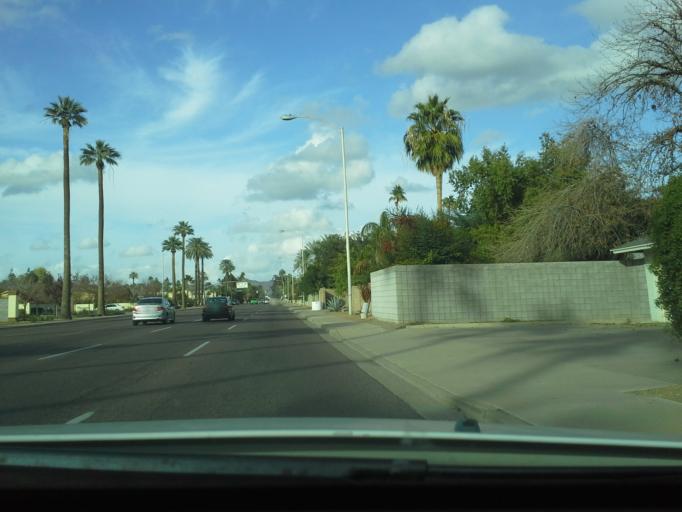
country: US
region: Arizona
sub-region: Maricopa County
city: Phoenix
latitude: 33.5278
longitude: -112.0824
